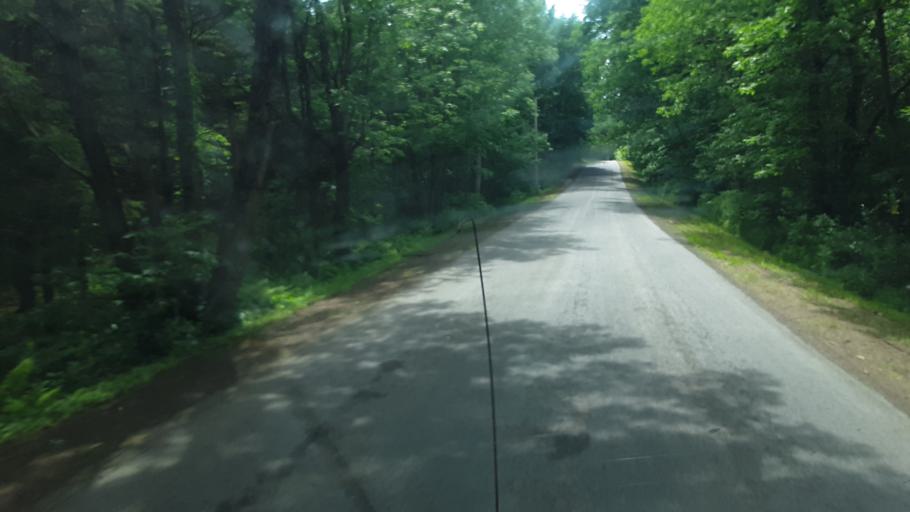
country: US
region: New York
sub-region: Oneida County
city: Rome
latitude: 43.3933
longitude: -75.5118
